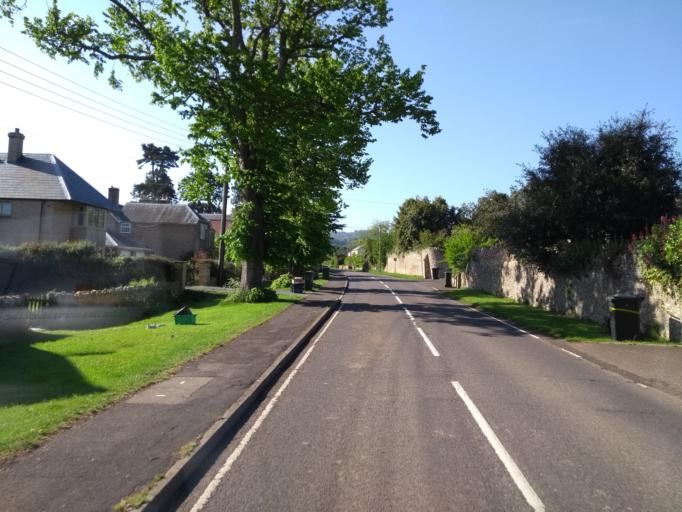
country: GB
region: England
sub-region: Somerset
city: Taunton
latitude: 50.9712
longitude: -3.0953
